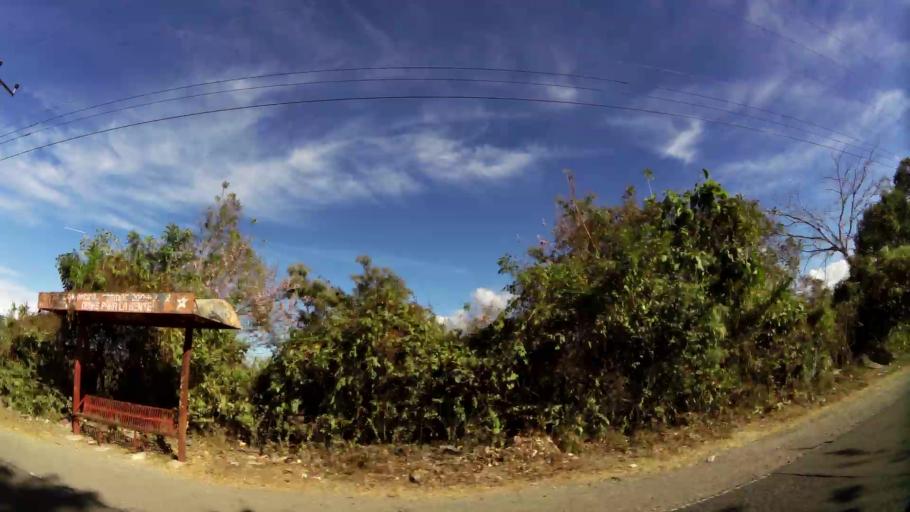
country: SV
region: Cuscatlan
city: Tecoluca
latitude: 13.8169
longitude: -89.0339
